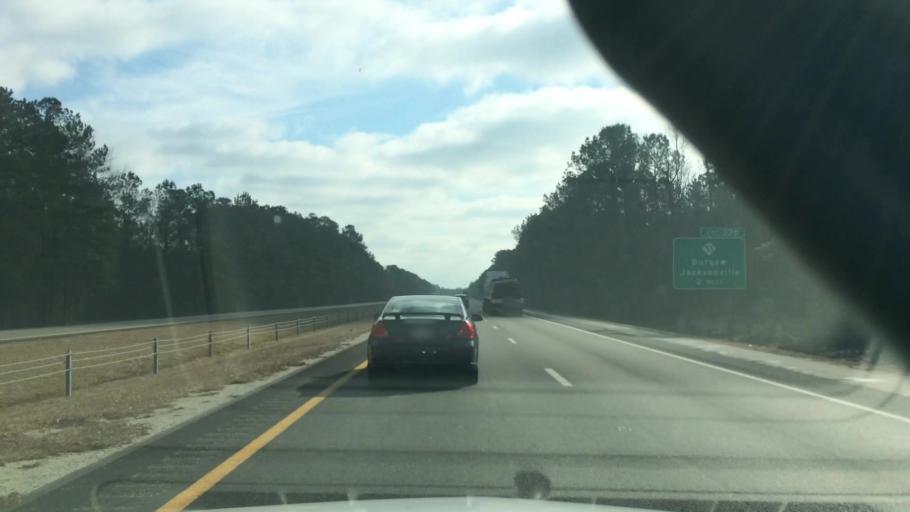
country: US
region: North Carolina
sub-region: Pender County
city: Burgaw
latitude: 34.6039
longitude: -77.9147
